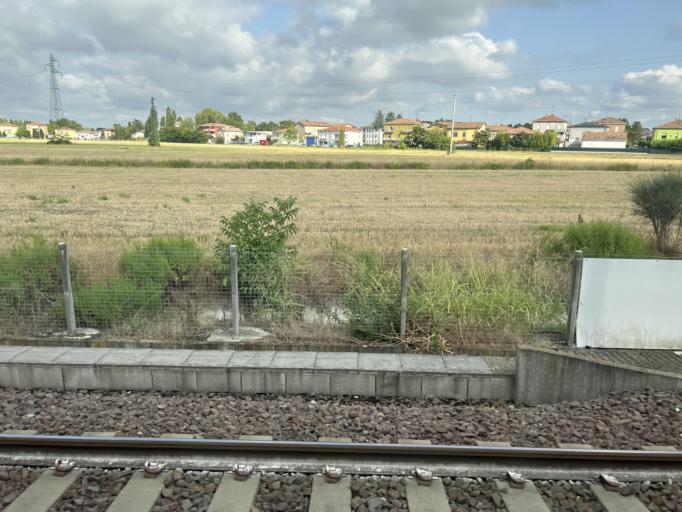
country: IT
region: Emilia-Romagna
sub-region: Provincia di Parma
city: Parma
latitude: 44.8170
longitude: 10.3478
